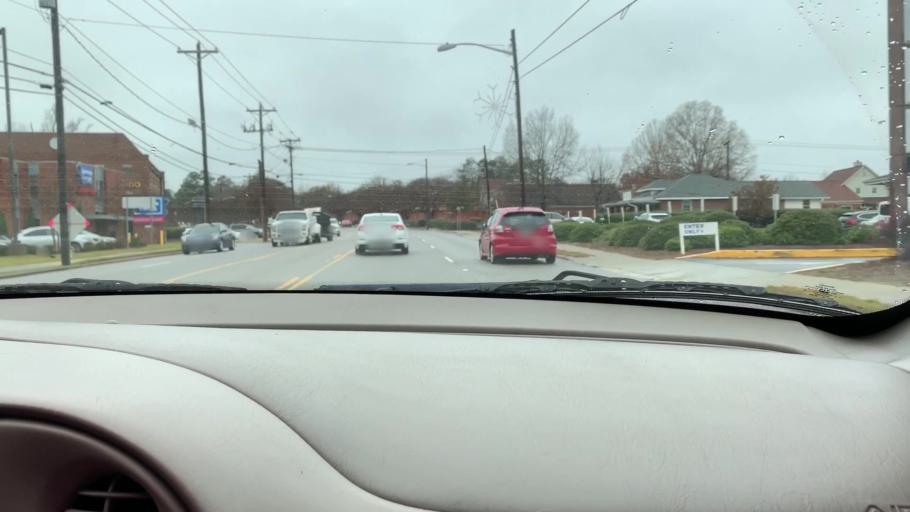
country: US
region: South Carolina
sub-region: Richland County
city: Forest Acres
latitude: 34.0206
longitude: -80.9727
